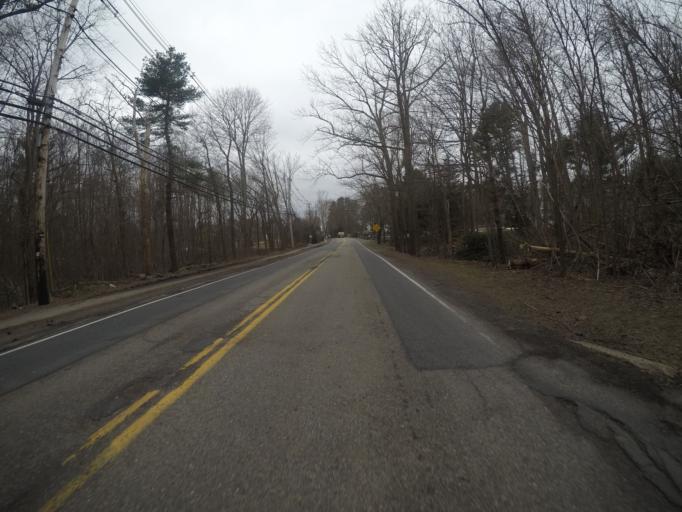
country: US
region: Massachusetts
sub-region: Bristol County
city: Easton
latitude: 42.0332
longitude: -71.1092
